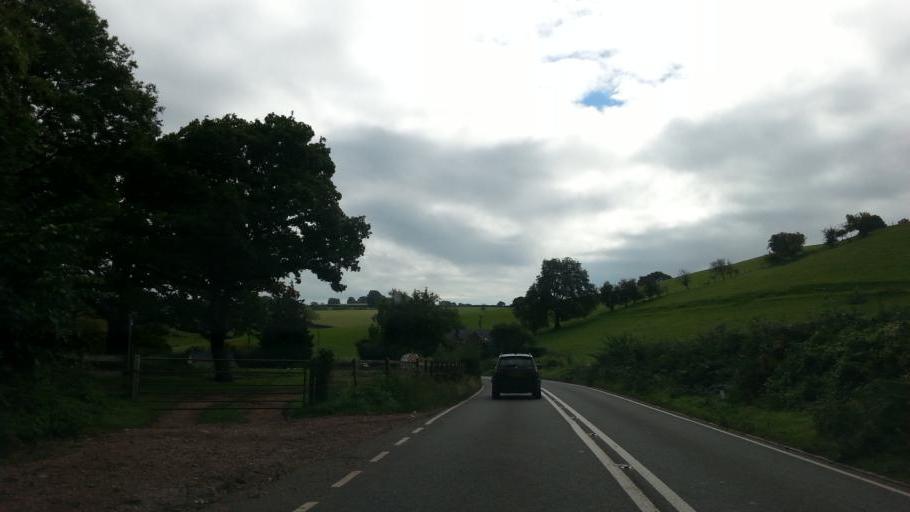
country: GB
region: England
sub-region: Gloucestershire
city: Mitcheldean
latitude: 51.8855
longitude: -2.4796
